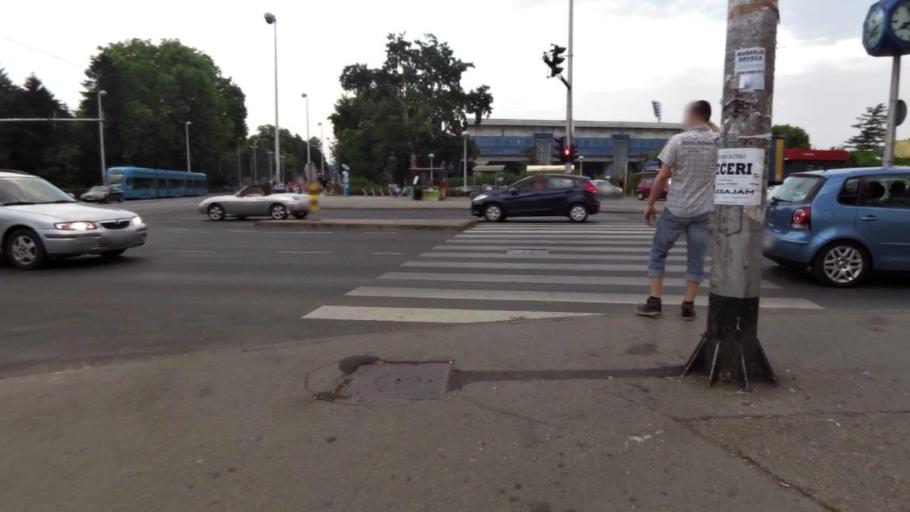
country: HR
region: Grad Zagreb
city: Zagreb
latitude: 45.8186
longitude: 16.0128
